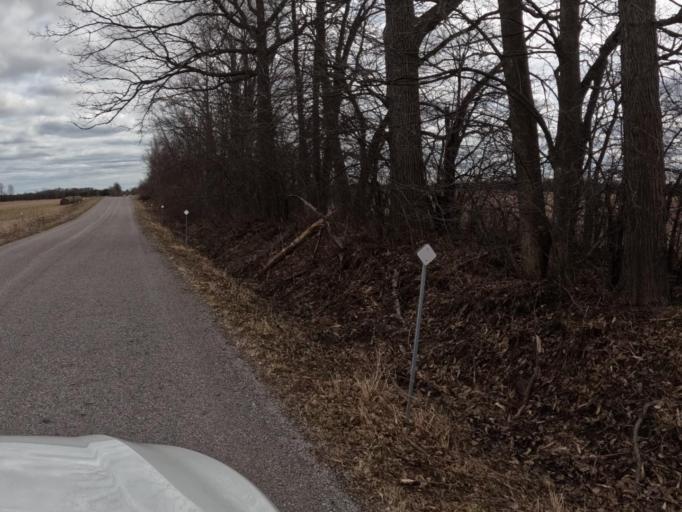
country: CA
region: Ontario
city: Norfolk County
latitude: 42.8635
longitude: -80.1749
